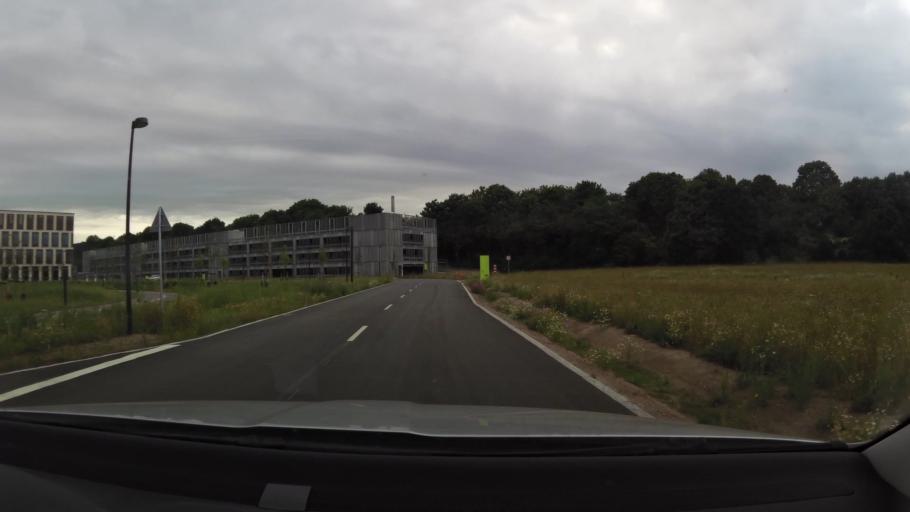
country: DK
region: Capital Region
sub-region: Lyngby-Tarbaek Kommune
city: Kongens Lyngby
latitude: 55.7866
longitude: 12.5316
